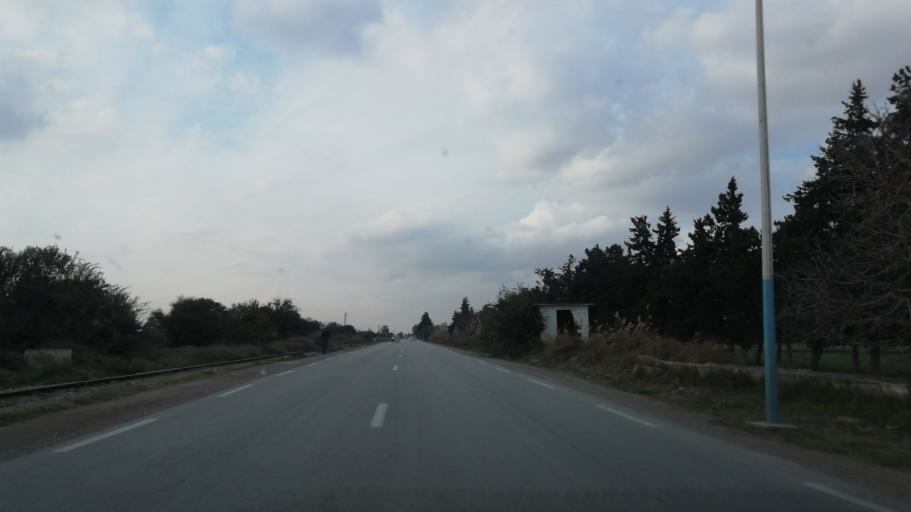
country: DZ
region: Mascara
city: Sig
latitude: 35.6578
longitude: 0.0122
